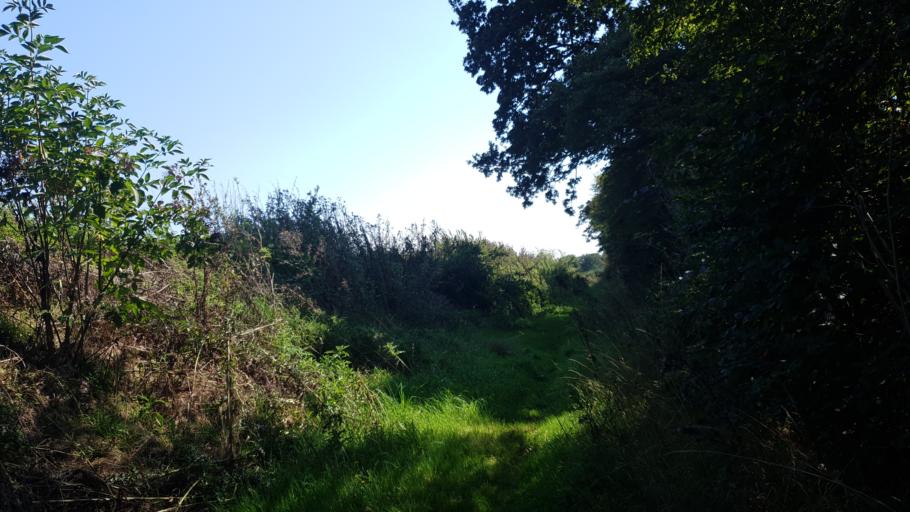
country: GB
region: England
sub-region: Essex
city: Colchester
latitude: 51.9235
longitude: 0.9488
